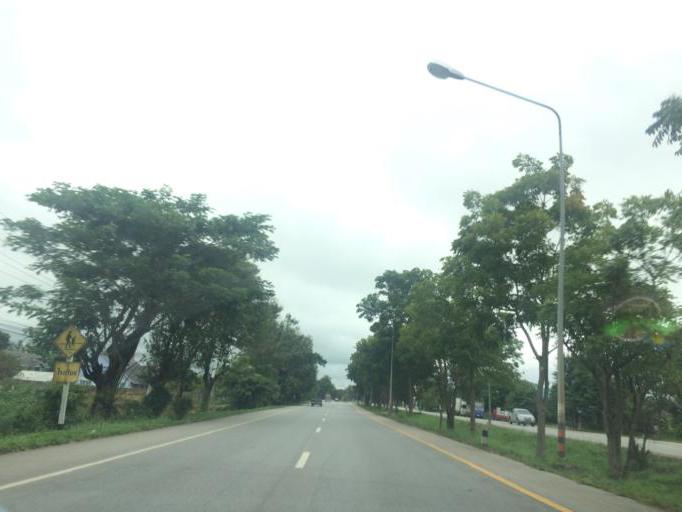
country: TH
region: Chiang Rai
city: Mae Lao
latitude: 19.7968
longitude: 99.7512
